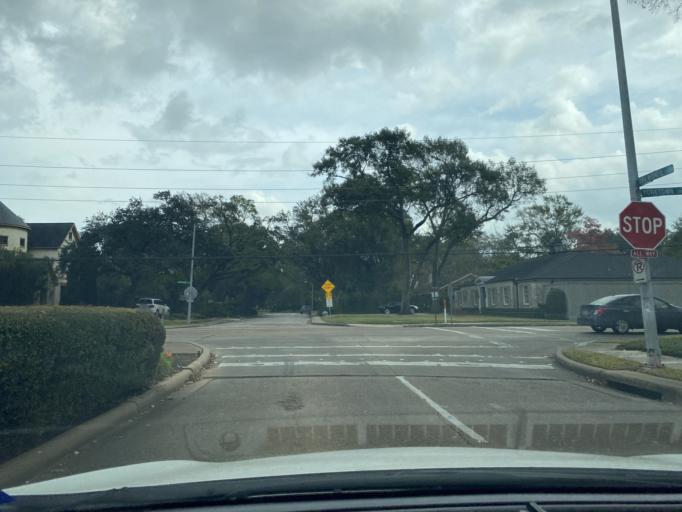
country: US
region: Texas
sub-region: Harris County
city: Hunters Creek Village
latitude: 29.7459
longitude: -95.4709
